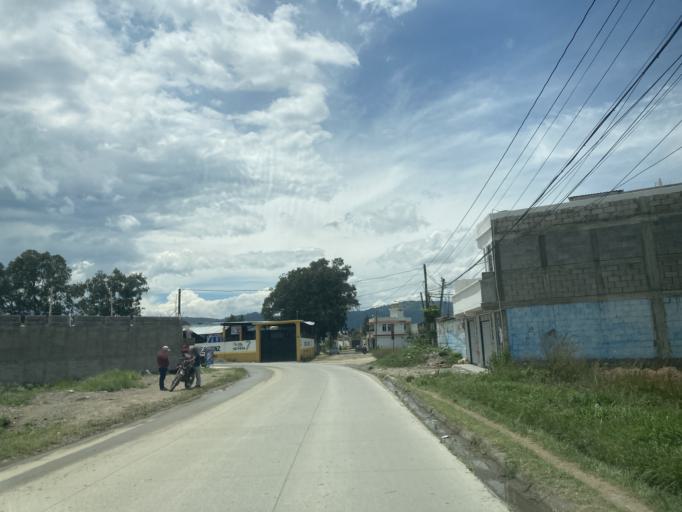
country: GT
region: Huehuetenango
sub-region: Municipio de Huehuetenango
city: Huehuetenango
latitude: 15.3247
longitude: -91.4953
